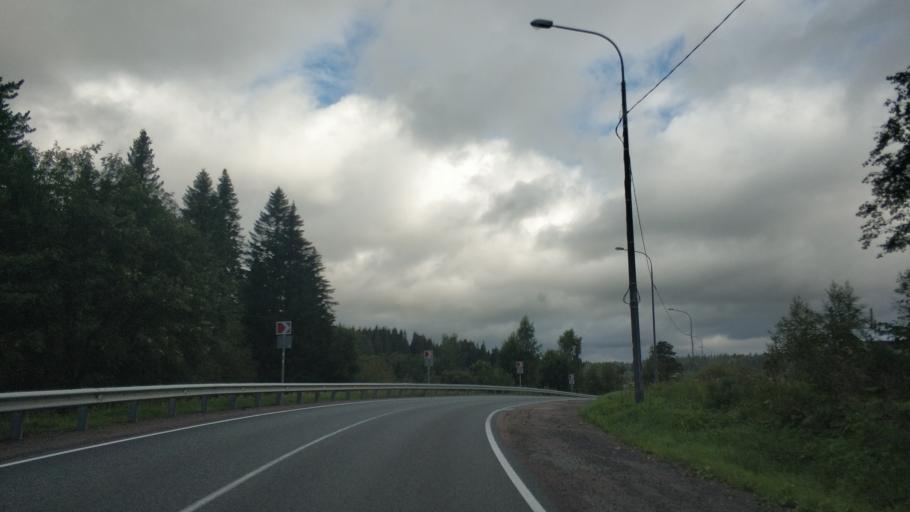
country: RU
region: Republic of Karelia
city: Khelyulya
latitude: 61.7551
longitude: 30.6567
